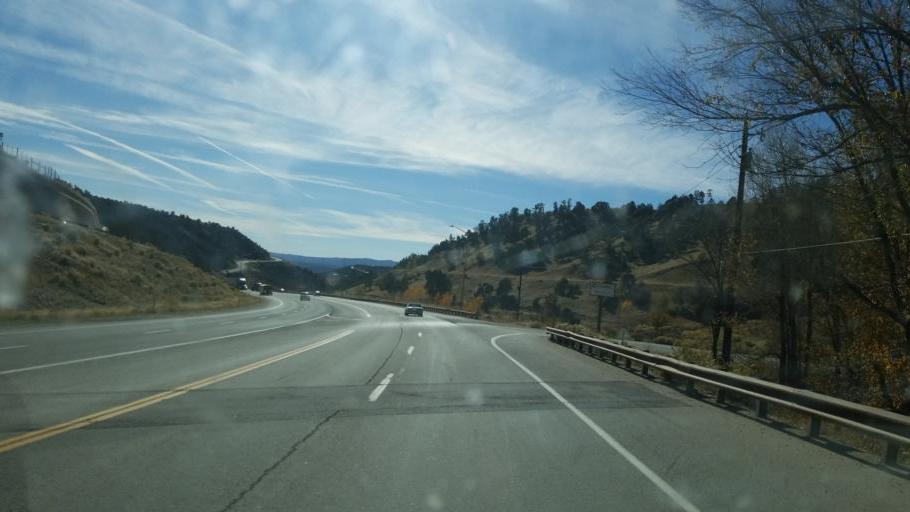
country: US
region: Colorado
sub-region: La Plata County
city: Durango
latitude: 37.2264
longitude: -107.8427
